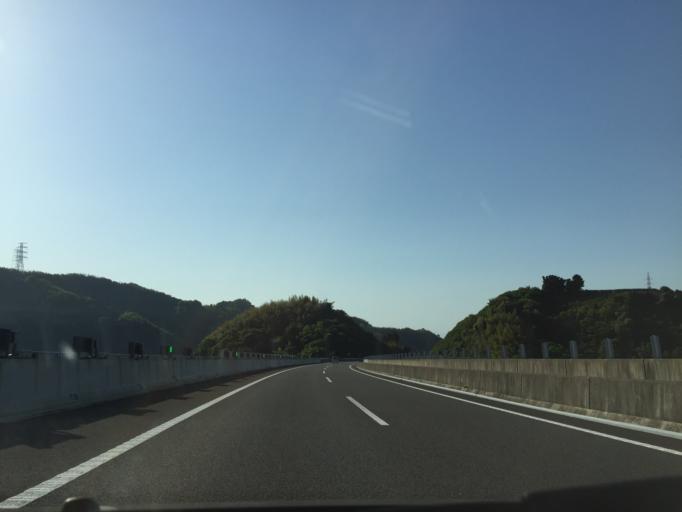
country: JP
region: Shizuoka
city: Shizuoka-shi
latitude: 35.0694
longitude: 138.4772
